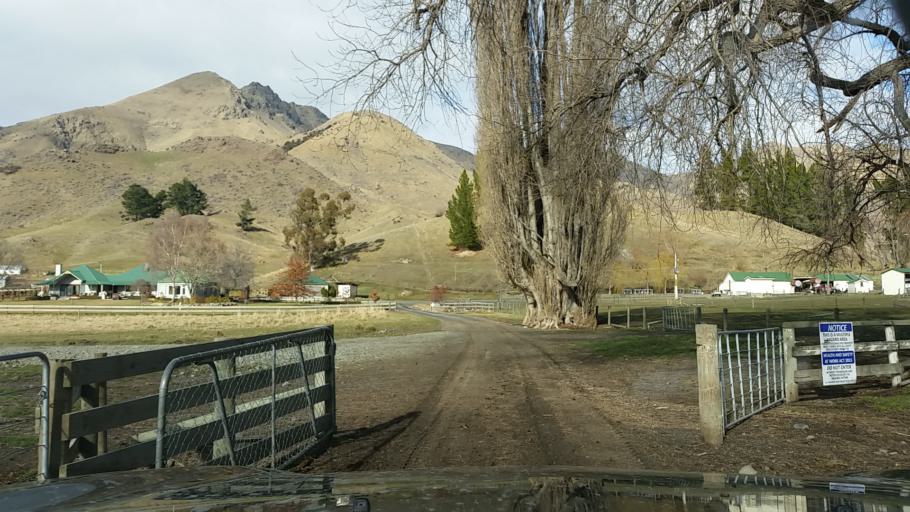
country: NZ
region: Canterbury
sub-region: Kaikoura District
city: Kaikoura
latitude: -42.0464
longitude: 173.3780
